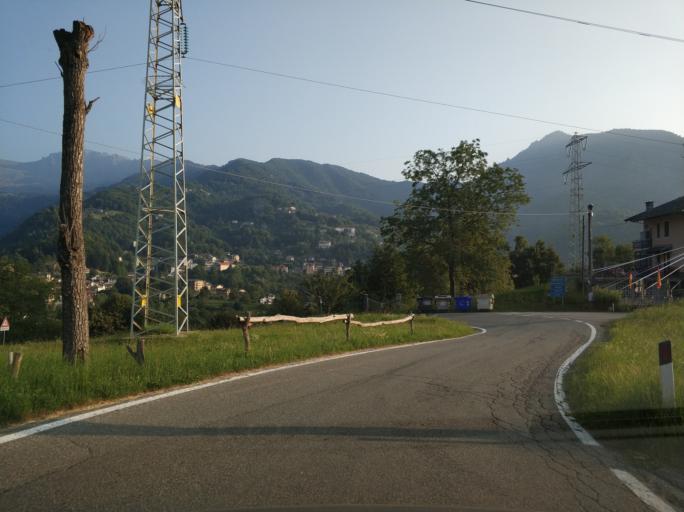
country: IT
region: Piedmont
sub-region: Provincia di Torino
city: Viu
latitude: 45.2301
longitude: 7.3756
